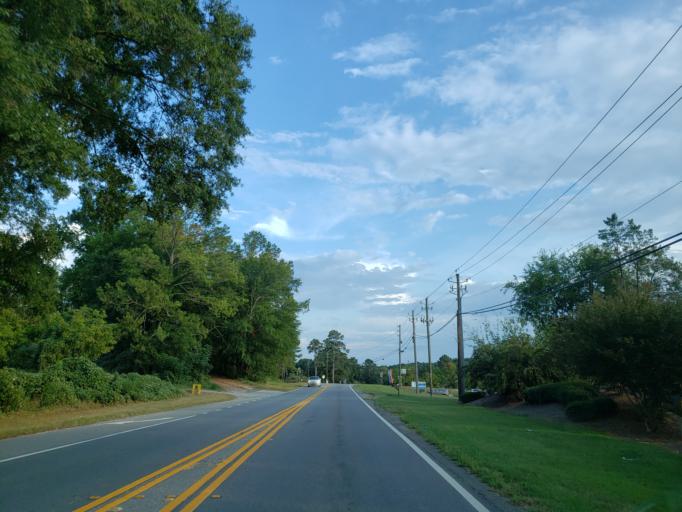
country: US
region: Georgia
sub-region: Bartow County
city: Cartersville
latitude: 34.2260
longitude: -84.8565
